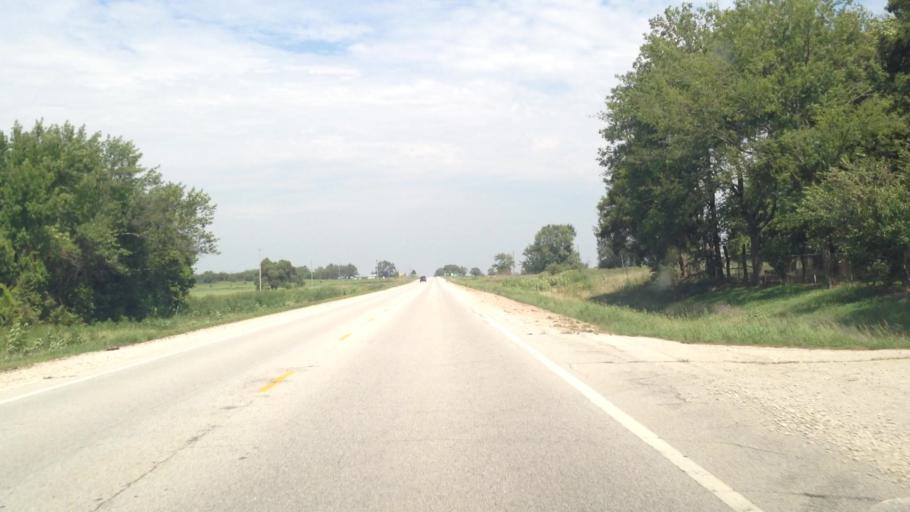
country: US
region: Kansas
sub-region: Neosho County
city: Erie
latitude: 37.4673
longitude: -95.2694
